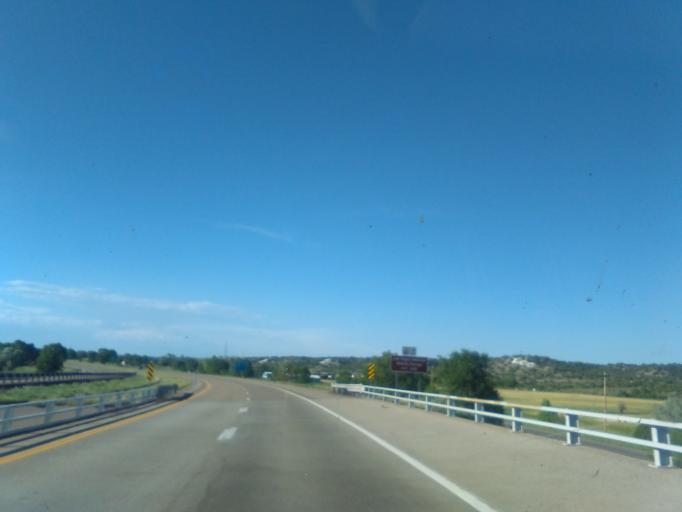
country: US
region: New Mexico
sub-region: San Miguel County
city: Las Vegas
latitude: 35.5756
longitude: -105.2121
